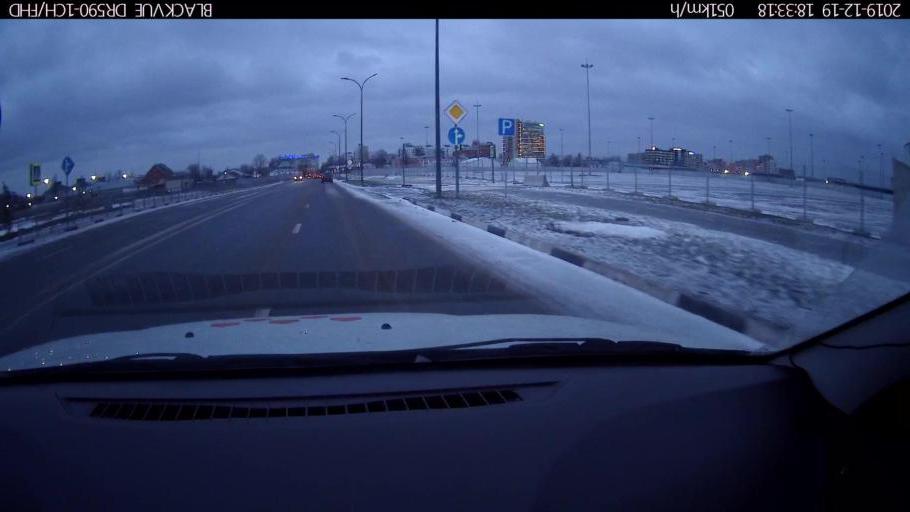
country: RU
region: Nizjnij Novgorod
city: Nizhniy Novgorod
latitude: 56.3348
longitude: 43.9700
